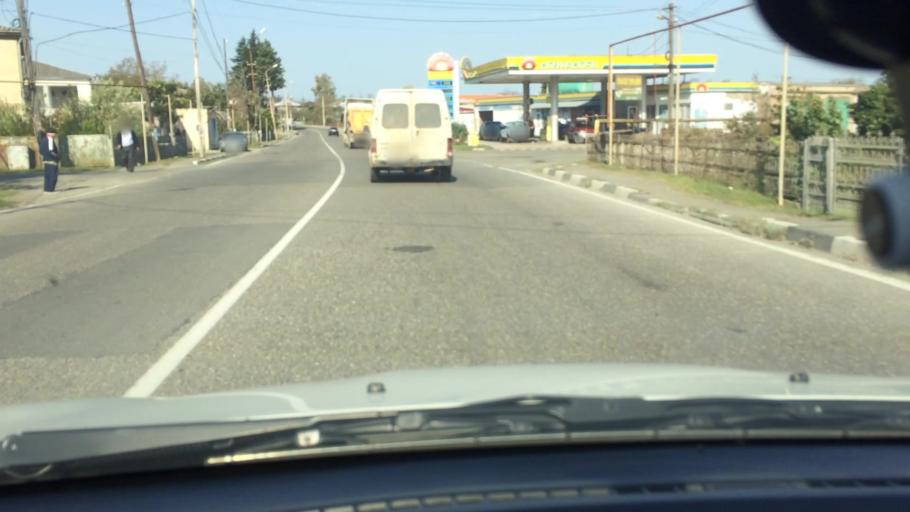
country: GE
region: Guria
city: Lanchkhuti
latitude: 42.0817
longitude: 42.0488
